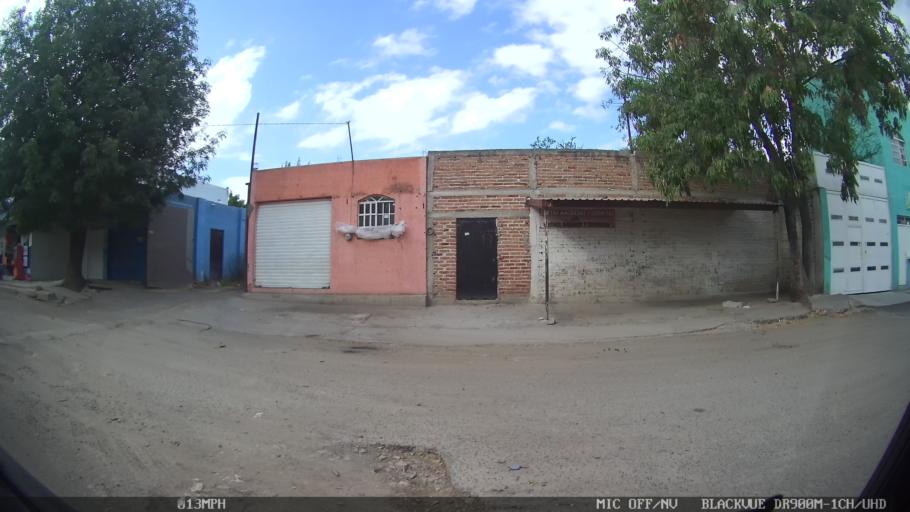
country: MX
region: Jalisco
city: Tonala
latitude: 20.6595
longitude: -103.2372
